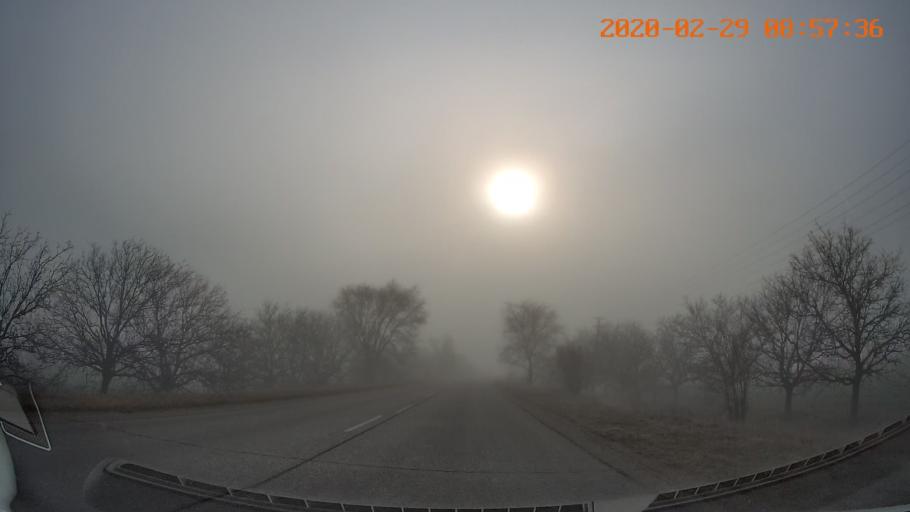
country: MD
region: Telenesti
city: Tiraspolul Nou
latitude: 46.9271
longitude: 29.6287
